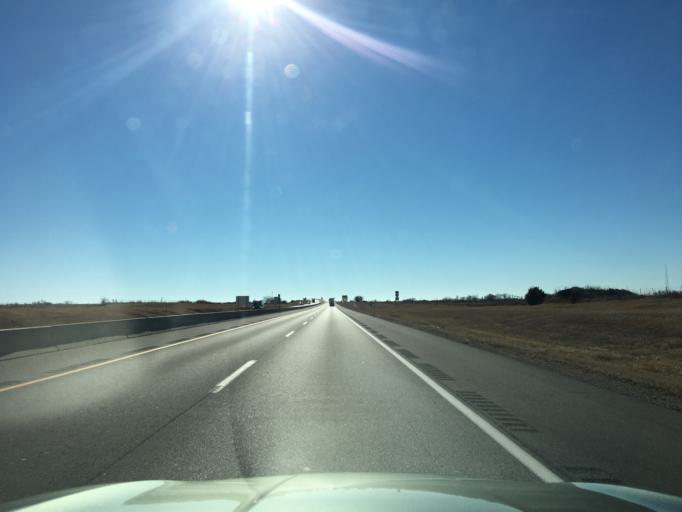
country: US
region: Kansas
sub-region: Sumner County
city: Wellington
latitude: 37.2746
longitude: -97.3404
